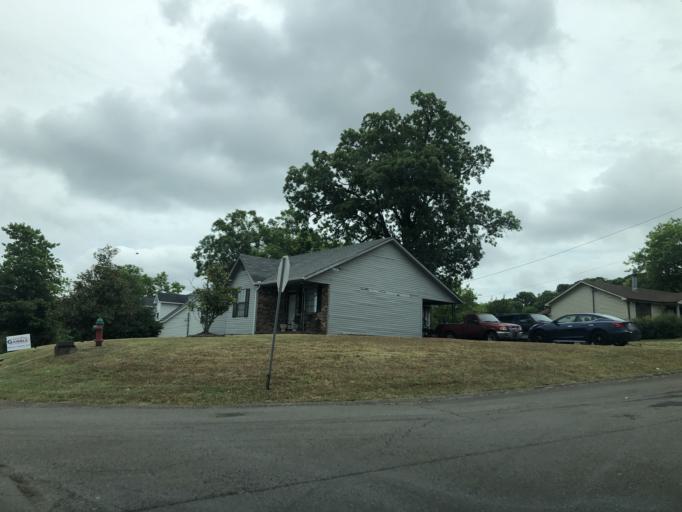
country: US
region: Tennessee
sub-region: Davidson County
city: Goodlettsville
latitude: 36.2555
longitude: -86.7654
